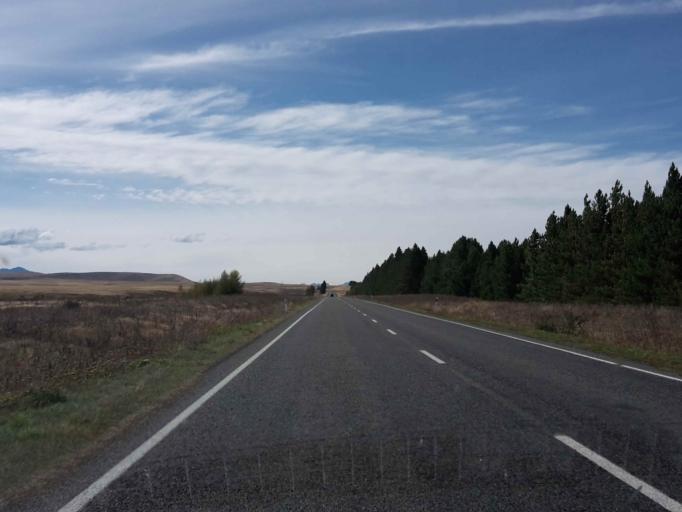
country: NZ
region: Canterbury
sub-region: Timaru District
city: Pleasant Point
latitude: -44.0604
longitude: 170.3669
